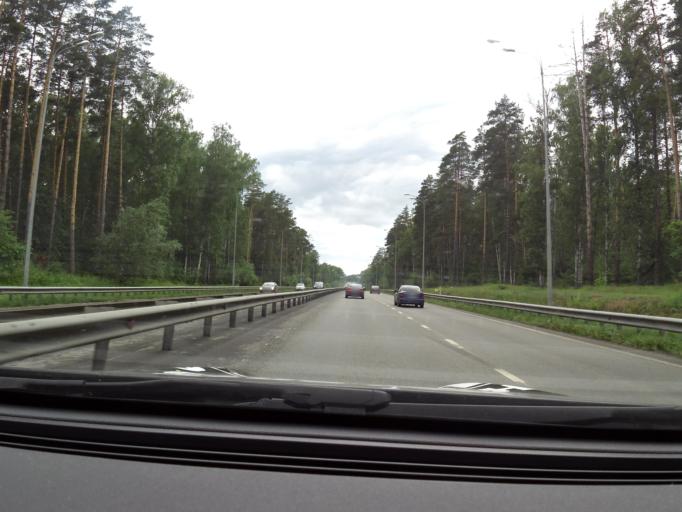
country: RU
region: Tatarstan
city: Staroye Arakchino
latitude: 55.8420
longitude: 48.9449
